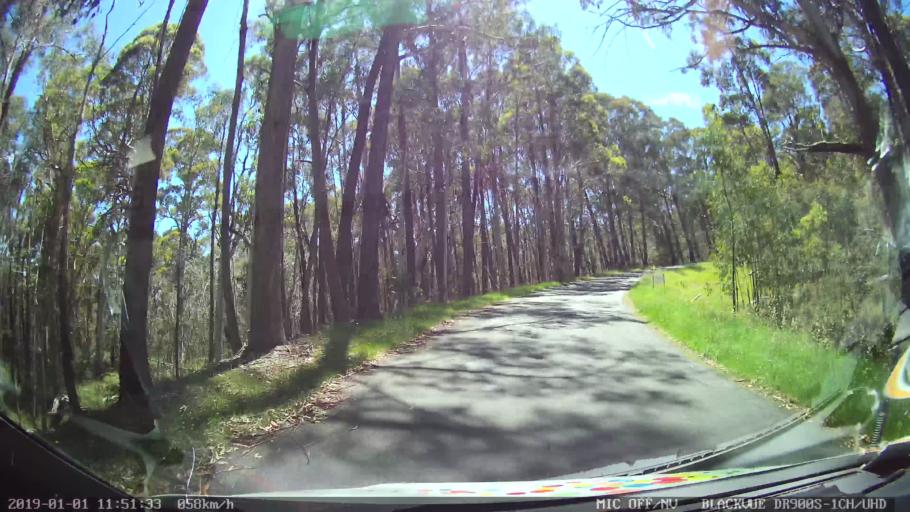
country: AU
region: New South Wales
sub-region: Snowy River
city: Jindabyne
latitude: -35.8844
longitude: 148.4310
